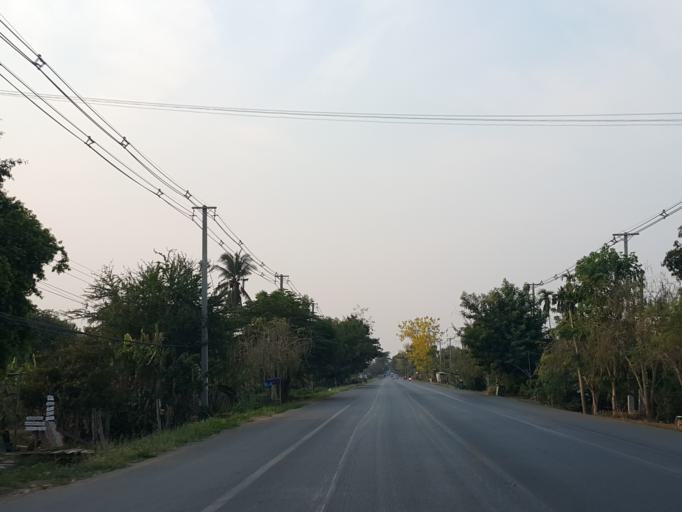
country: TH
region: Sukhothai
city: Si Samrong
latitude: 17.2361
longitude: 99.8582
